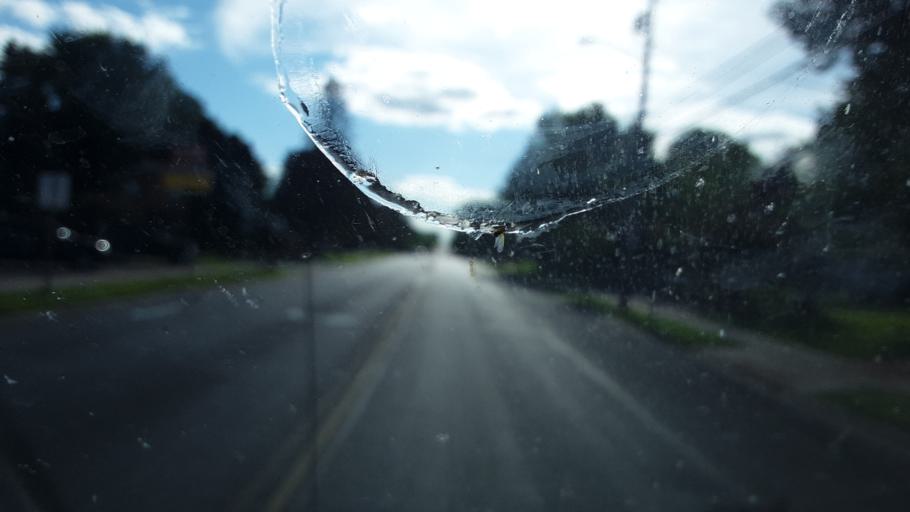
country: US
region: Wisconsin
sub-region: Wood County
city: Marshfield
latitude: 44.6556
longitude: -90.1855
